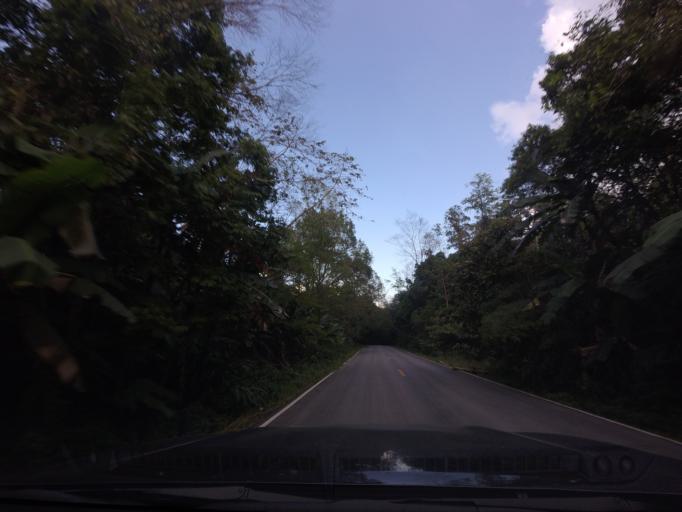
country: TH
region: Phetchabun
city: Lom Kao
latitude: 16.9431
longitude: 101.0383
